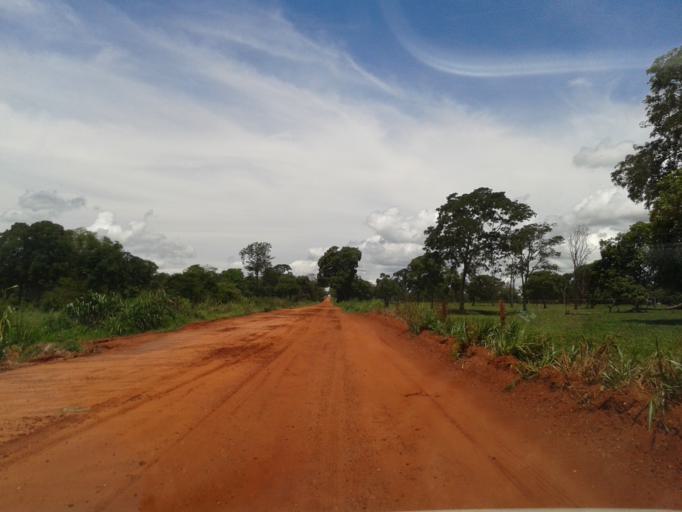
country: BR
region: Minas Gerais
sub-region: Santa Vitoria
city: Santa Vitoria
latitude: -19.1955
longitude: -50.6432
